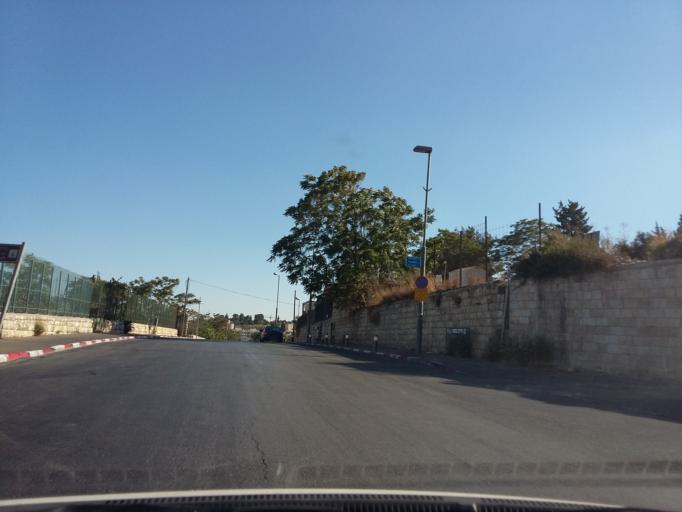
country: PS
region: West Bank
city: Old City
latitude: 31.7720
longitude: 35.2307
